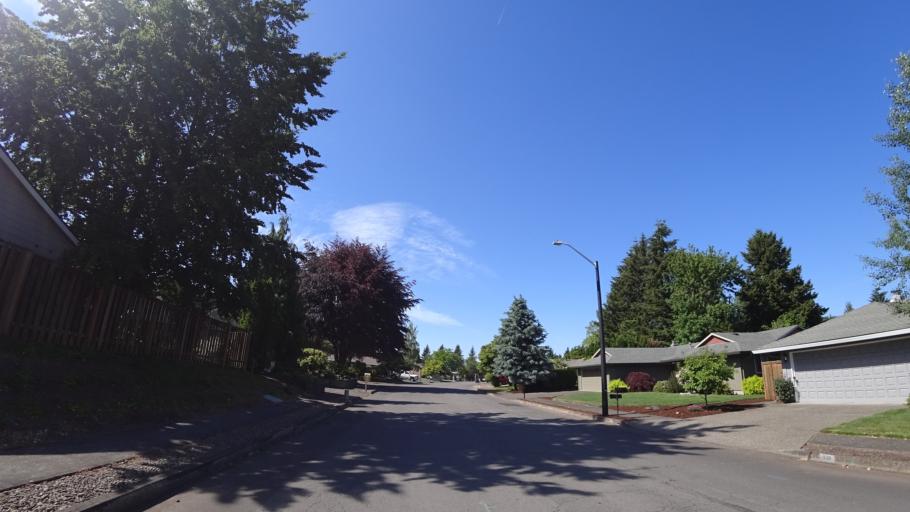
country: US
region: Oregon
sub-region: Multnomah County
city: Gresham
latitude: 45.4932
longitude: -122.4728
